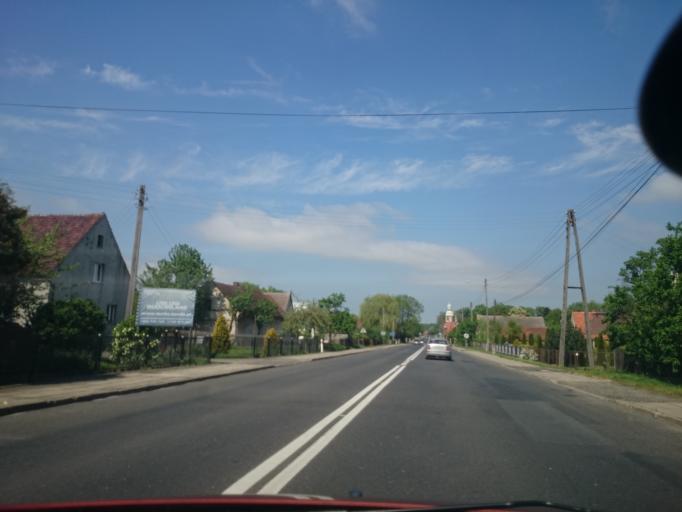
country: PL
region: Opole Voivodeship
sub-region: Powiat opolski
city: Dabrowa
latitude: 50.7207
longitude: 17.7667
